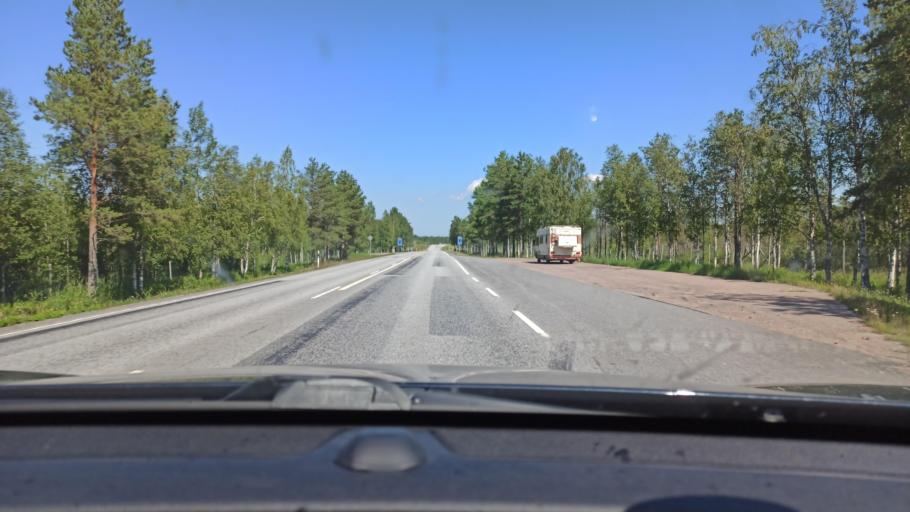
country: FI
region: Northern Ostrobothnia
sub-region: Oulu
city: Lumijoki
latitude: 64.7703
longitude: 25.2309
